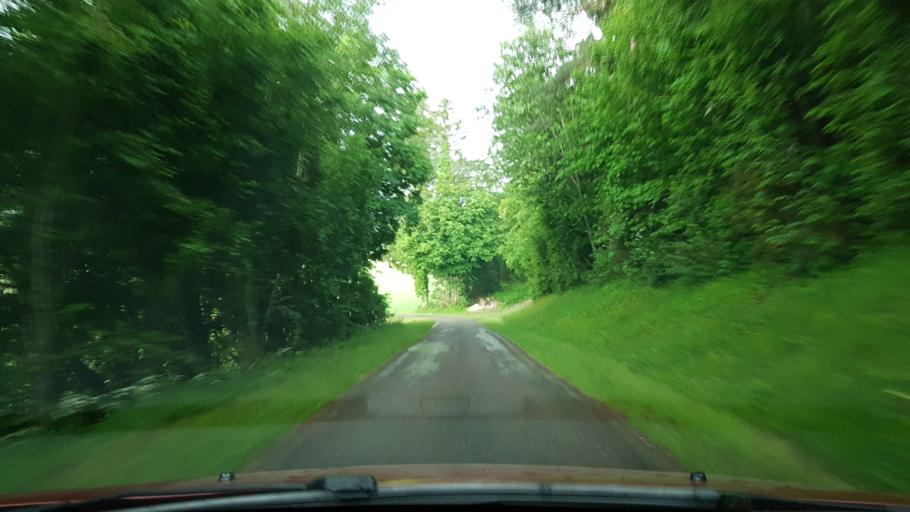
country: FR
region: Franche-Comte
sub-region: Departement du Jura
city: Clairvaux-les-Lacs
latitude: 46.5454
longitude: 5.6992
